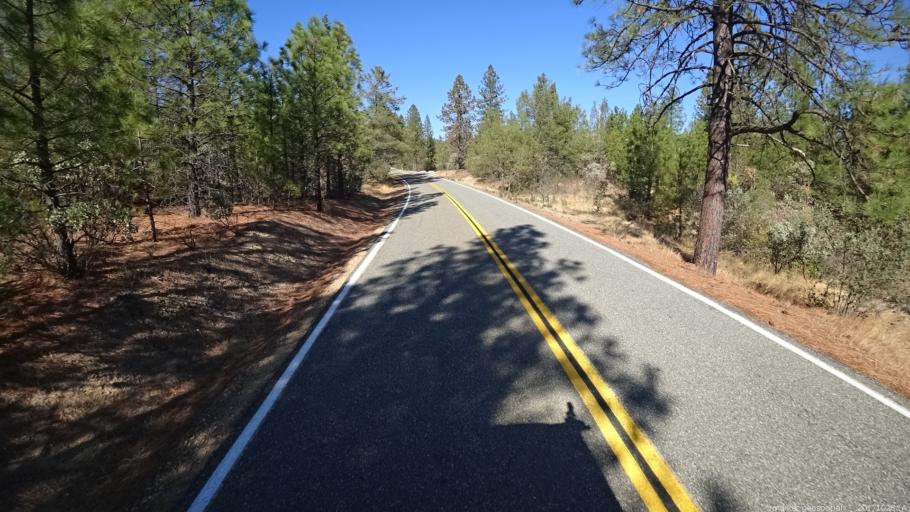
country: US
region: California
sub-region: Shasta County
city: Shasta
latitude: 40.6512
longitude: -122.4610
